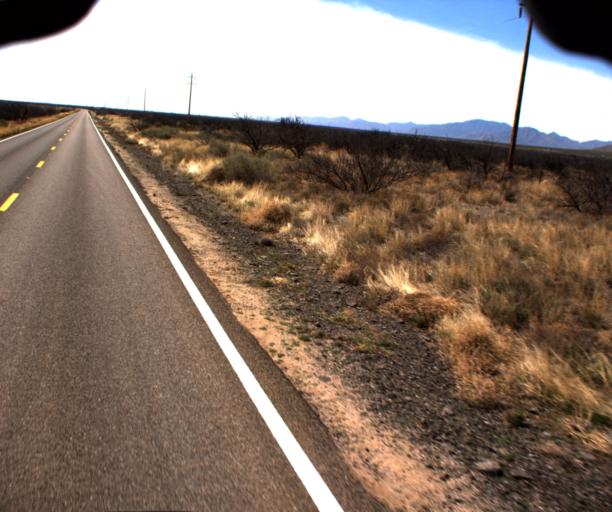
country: US
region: Arizona
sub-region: Cochise County
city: Willcox
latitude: 32.1535
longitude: -109.9378
